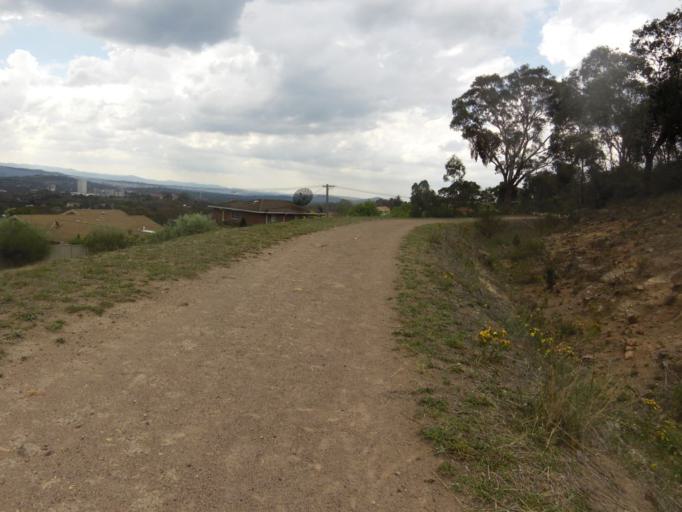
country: AU
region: Australian Capital Territory
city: Forrest
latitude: -35.3597
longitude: 149.1125
